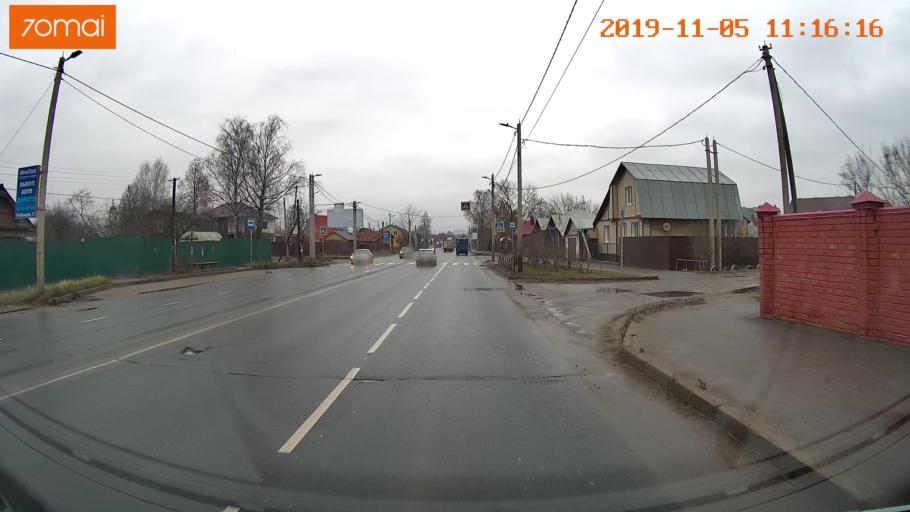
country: RU
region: Ivanovo
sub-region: Gorod Ivanovo
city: Ivanovo
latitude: 56.9835
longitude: 40.9535
